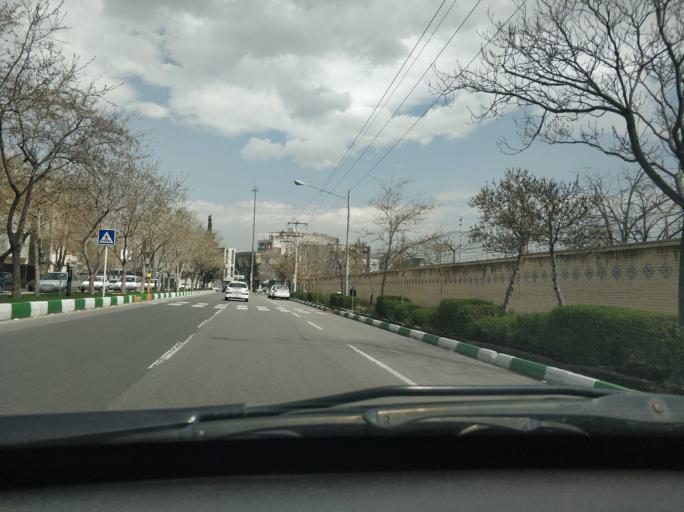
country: IR
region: Razavi Khorasan
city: Mashhad
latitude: 36.2835
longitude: 59.5779
